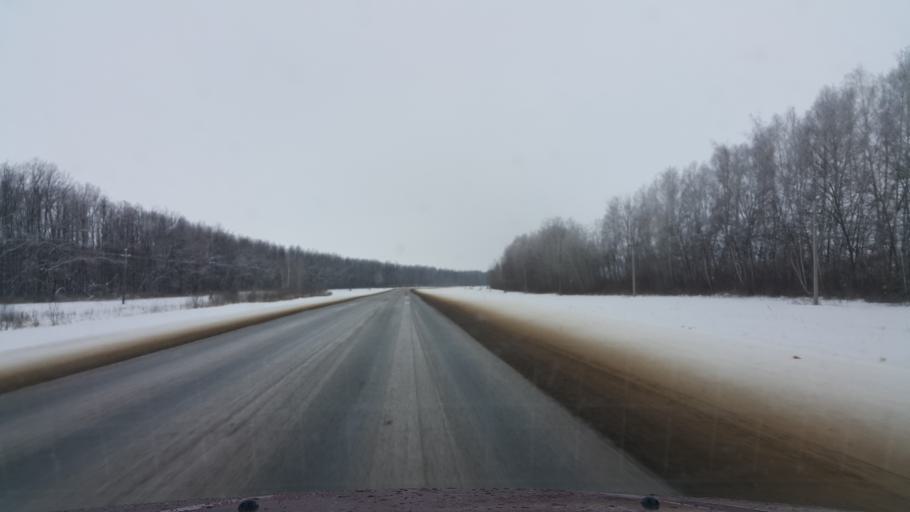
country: RU
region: Tambov
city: Bokino
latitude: 52.5943
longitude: 41.4452
